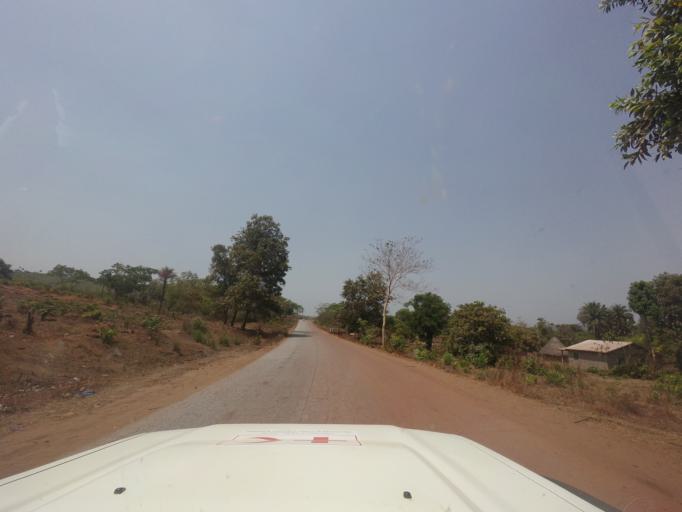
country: GN
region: Kindia
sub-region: Kindia
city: Kindia
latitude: 9.8500
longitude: -13.0905
